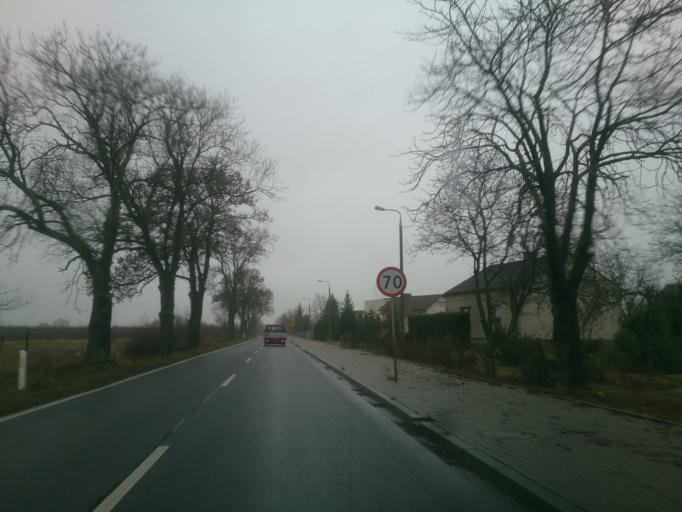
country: PL
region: Kujawsko-Pomorskie
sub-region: Powiat brodnicki
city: Brodnica
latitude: 53.1723
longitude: 19.3871
